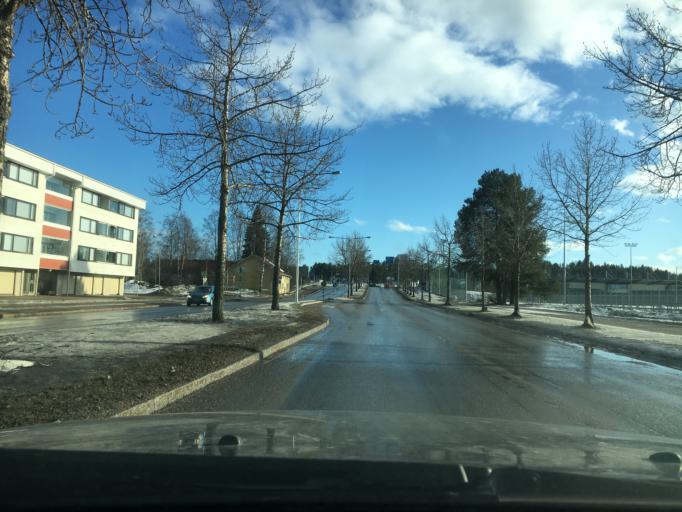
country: FI
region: Kainuu
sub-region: Kajaani
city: Kajaani
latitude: 64.2212
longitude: 27.7289
